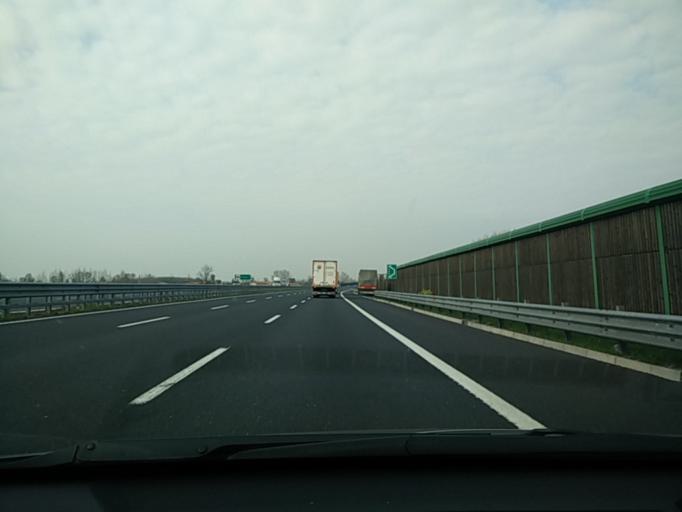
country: IT
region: Veneto
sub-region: Provincia di Venezia
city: Maerne
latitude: 45.5102
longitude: 12.1397
